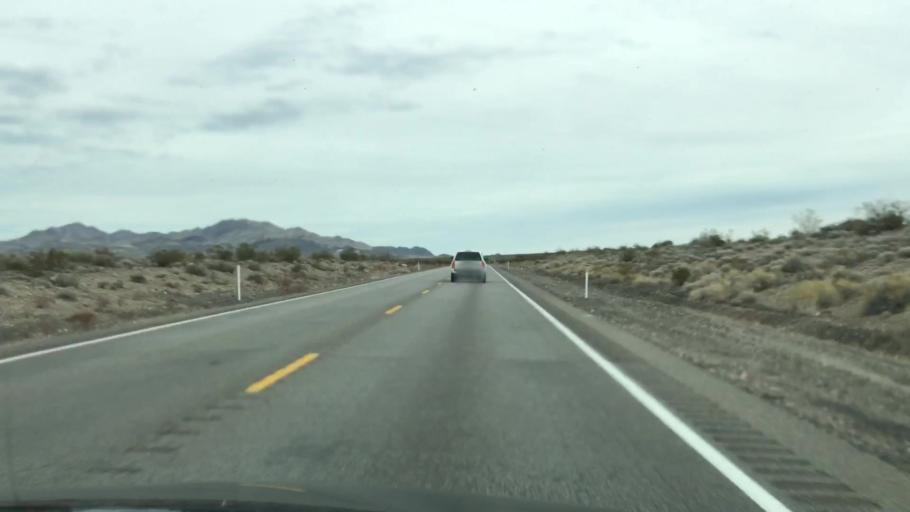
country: US
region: Nevada
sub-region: Nye County
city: Pahrump
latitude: 36.5887
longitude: -116.0491
